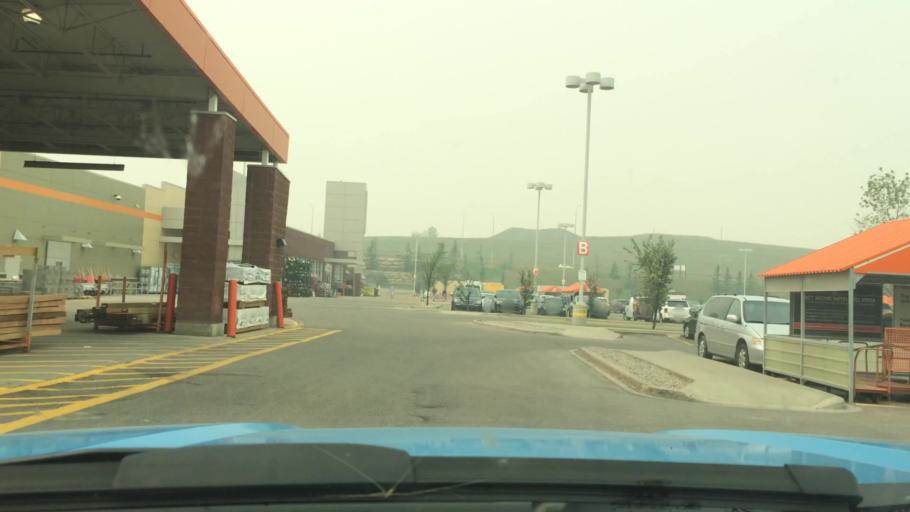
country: CA
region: Alberta
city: Calgary
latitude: 51.1552
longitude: -114.1600
